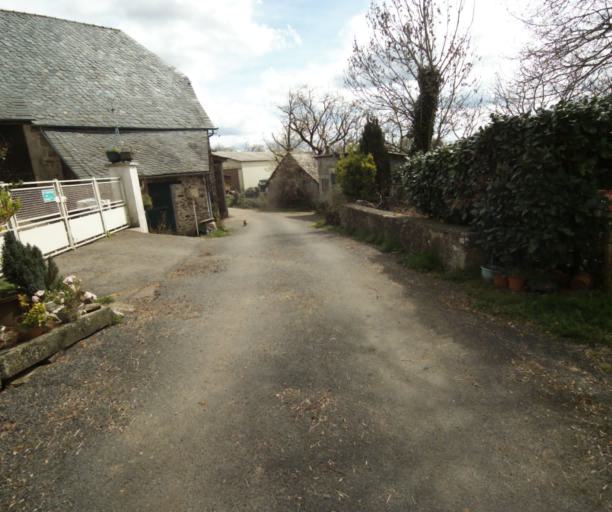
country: FR
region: Limousin
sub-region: Departement de la Correze
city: Laguenne
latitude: 45.2027
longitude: 1.8781
